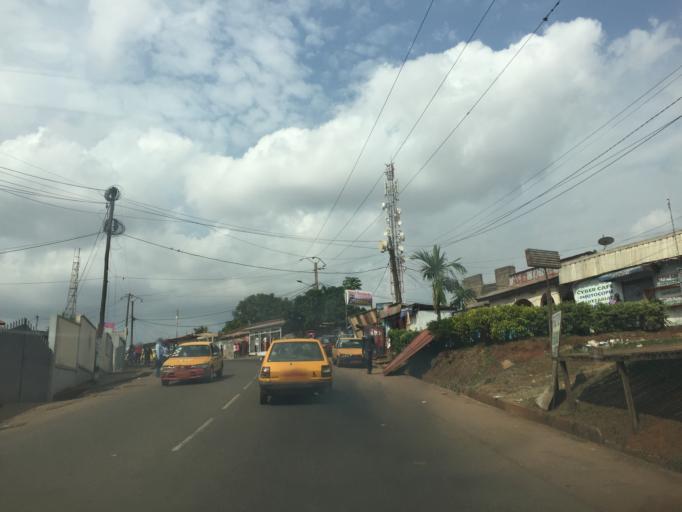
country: CM
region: Centre
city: Yaounde
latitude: 3.8555
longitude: 11.5026
